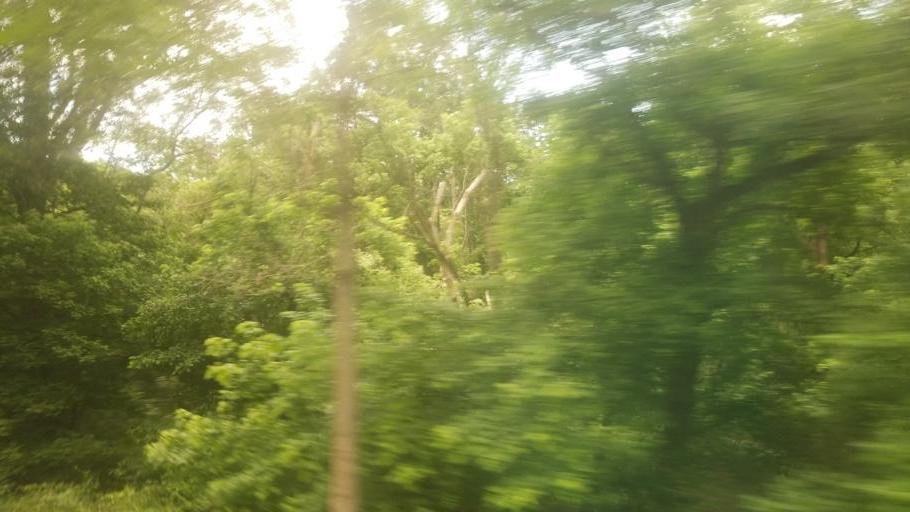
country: US
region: Maryland
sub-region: Frederick County
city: Brunswick
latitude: 39.3086
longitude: -77.5830
